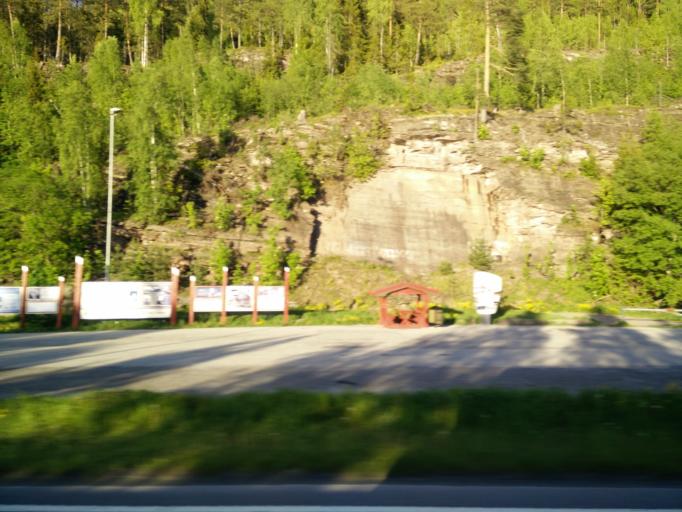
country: NO
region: Buskerud
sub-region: Hole
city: Vik
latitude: 60.0265
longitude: 10.2687
